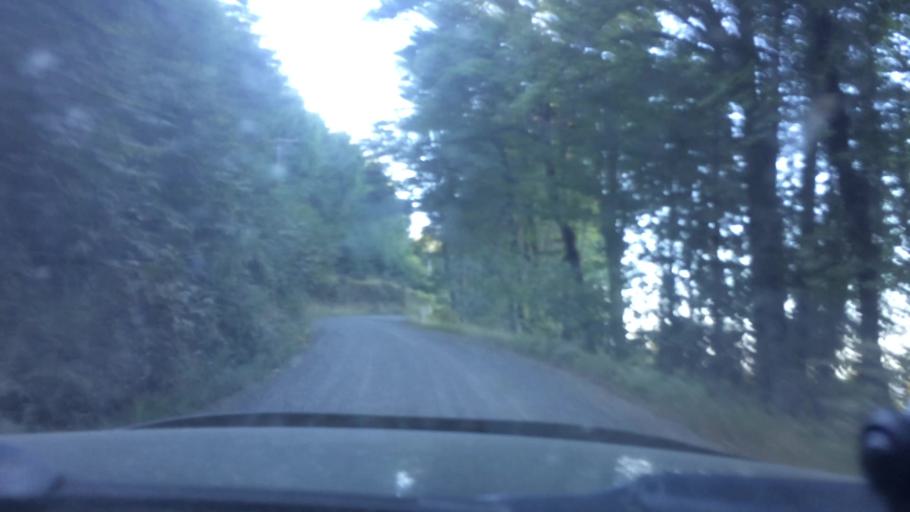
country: US
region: Oregon
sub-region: Yamhill County
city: Newberg
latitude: 45.3624
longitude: -122.9825
